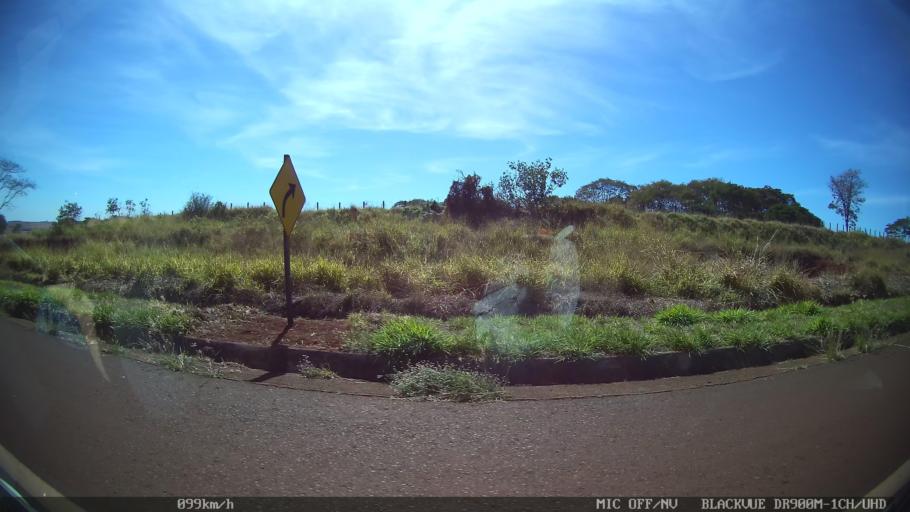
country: BR
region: Sao Paulo
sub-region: Nuporanga
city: Nuporanga
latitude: -20.5608
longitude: -47.6299
